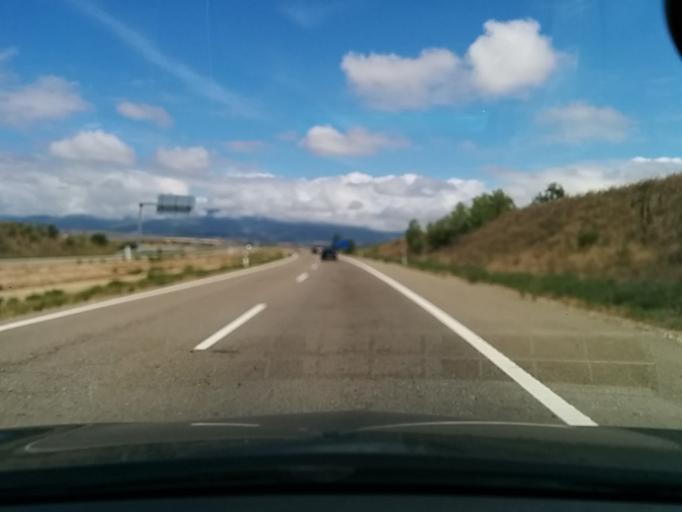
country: ES
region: Aragon
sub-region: Provincia de Huesca
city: Banastas
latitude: 42.1843
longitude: -0.4307
